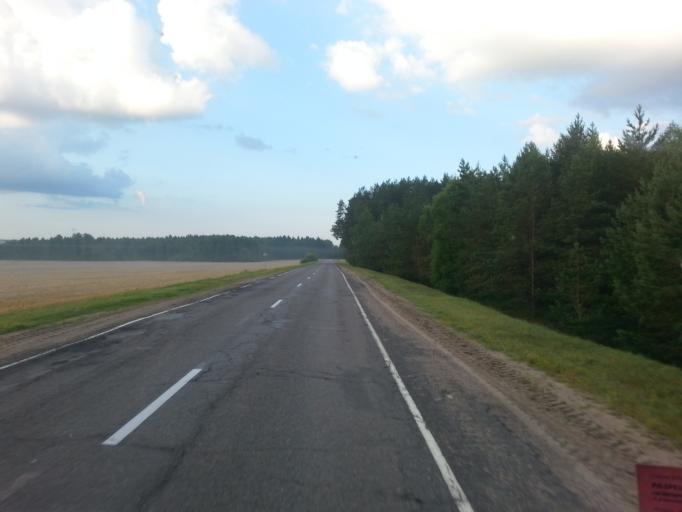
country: BY
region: Minsk
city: Il'ya
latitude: 54.5486
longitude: 27.2113
